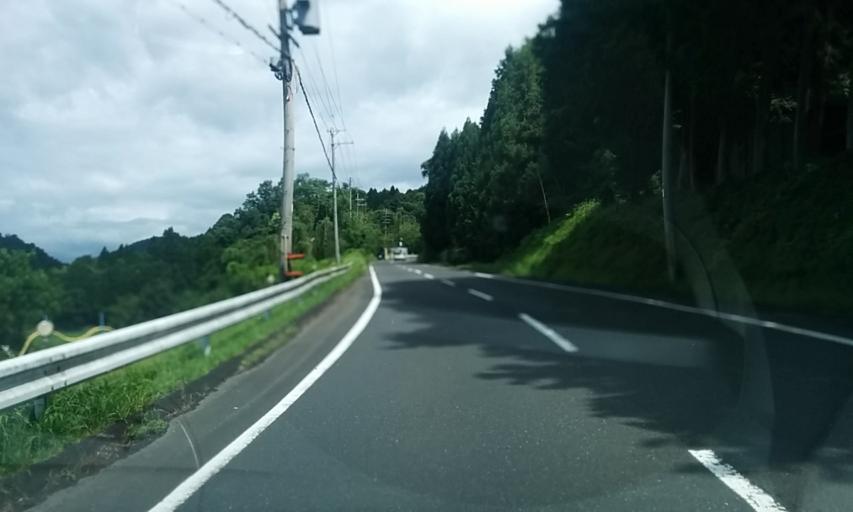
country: JP
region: Kyoto
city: Ayabe
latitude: 35.3525
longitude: 135.2716
